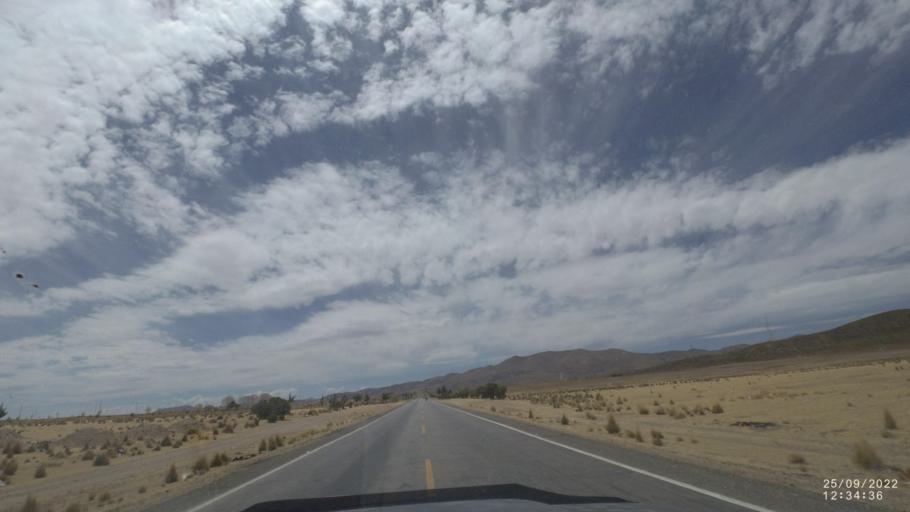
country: BO
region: Oruro
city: Machacamarca
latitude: -18.1732
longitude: -67.0133
